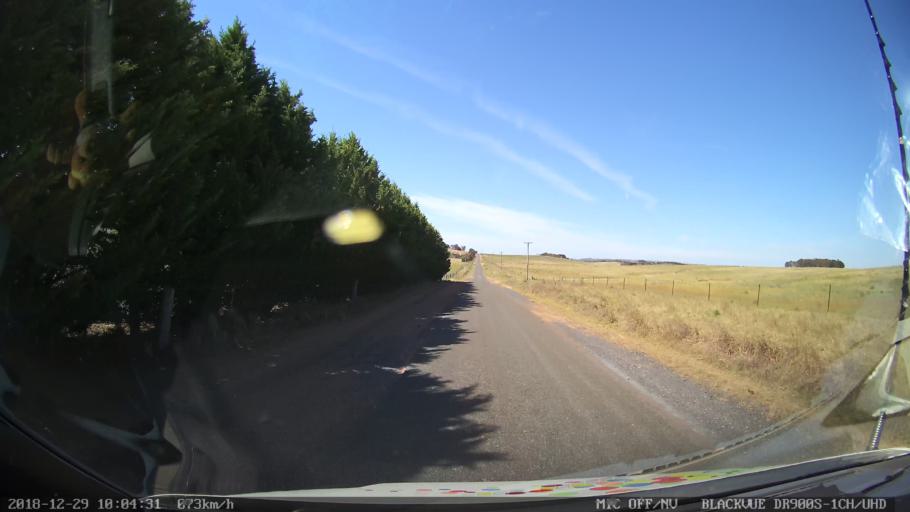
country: AU
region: New South Wales
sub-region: Goulburn Mulwaree
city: Goulburn
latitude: -34.8229
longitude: 149.4552
